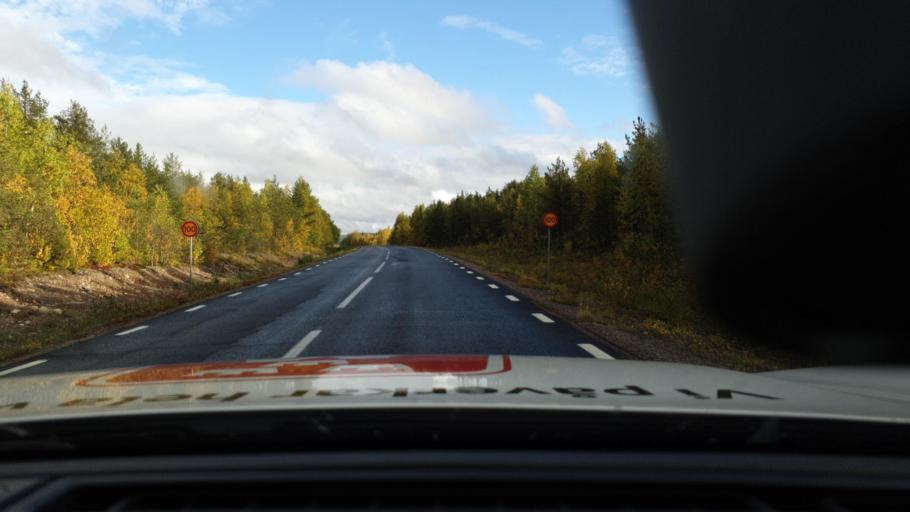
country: SE
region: Norrbotten
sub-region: Overkalix Kommun
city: OEverkalix
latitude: 66.9238
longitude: 22.7427
